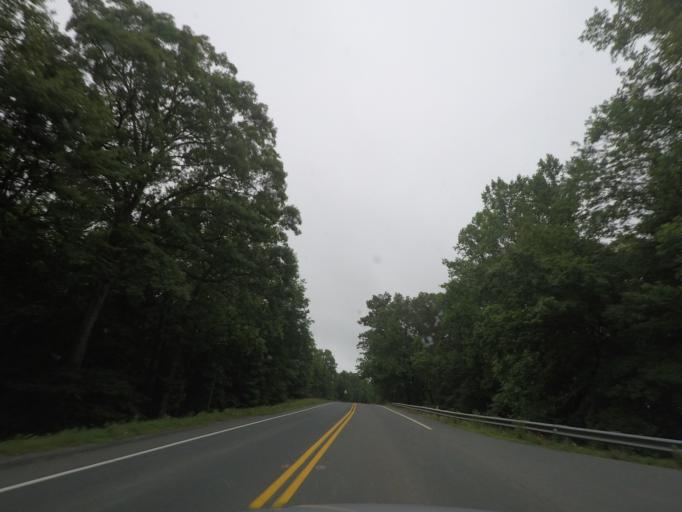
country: US
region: Virginia
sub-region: Fluvanna County
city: Weber City
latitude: 37.7269
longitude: -78.2974
